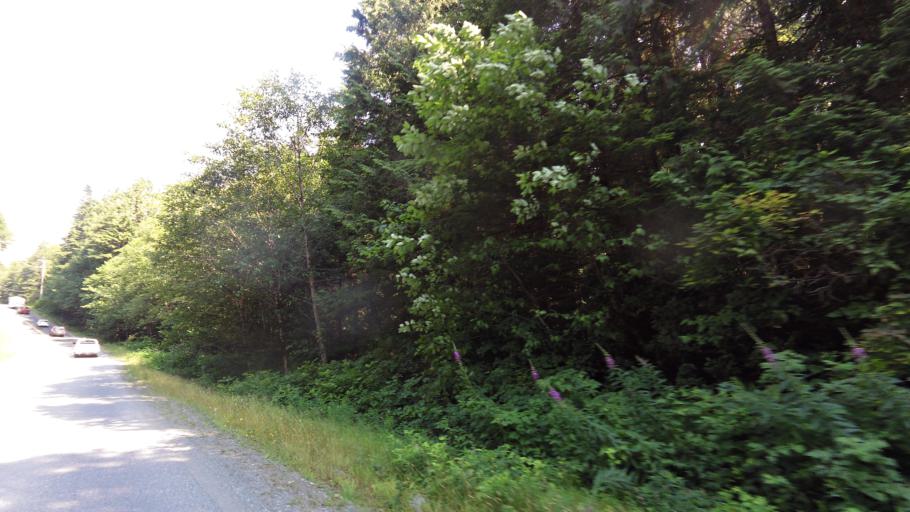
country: CA
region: British Columbia
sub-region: Regional District of Alberni-Clayoquot
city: Tofino
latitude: 49.0917
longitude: -125.8435
